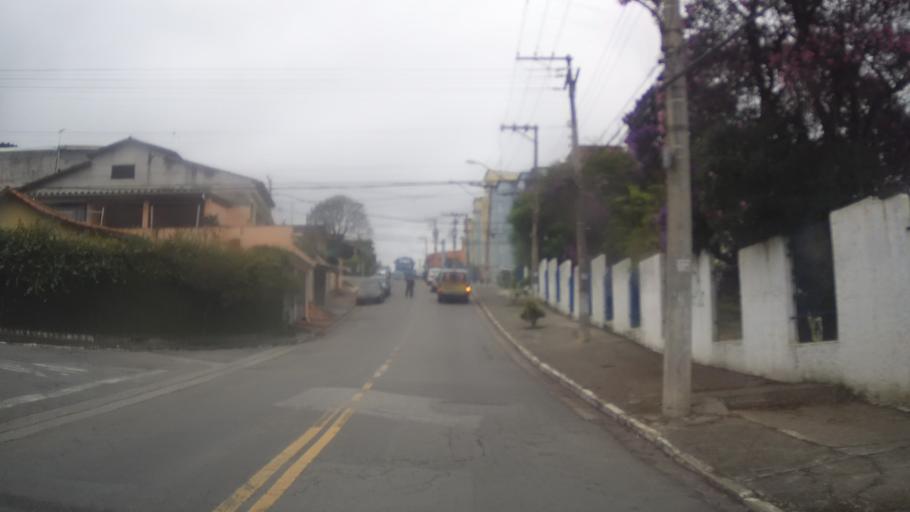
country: BR
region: Sao Paulo
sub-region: Guarulhos
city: Guarulhos
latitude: -23.4400
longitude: -46.5139
